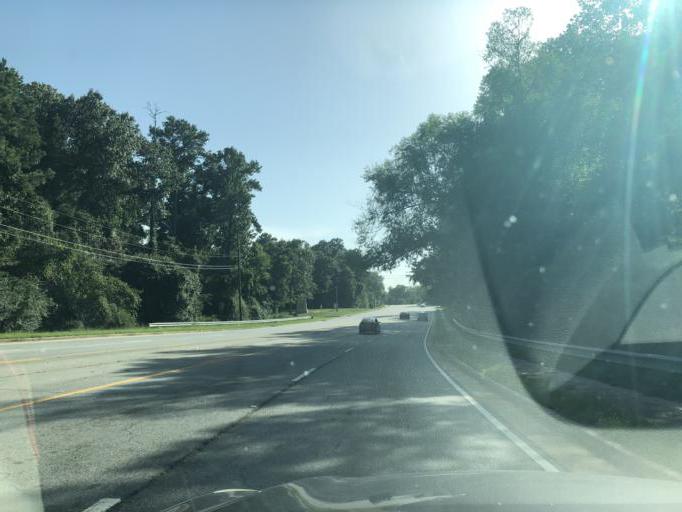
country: US
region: Georgia
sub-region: Muscogee County
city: Columbus
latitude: 32.5022
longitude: -84.9002
